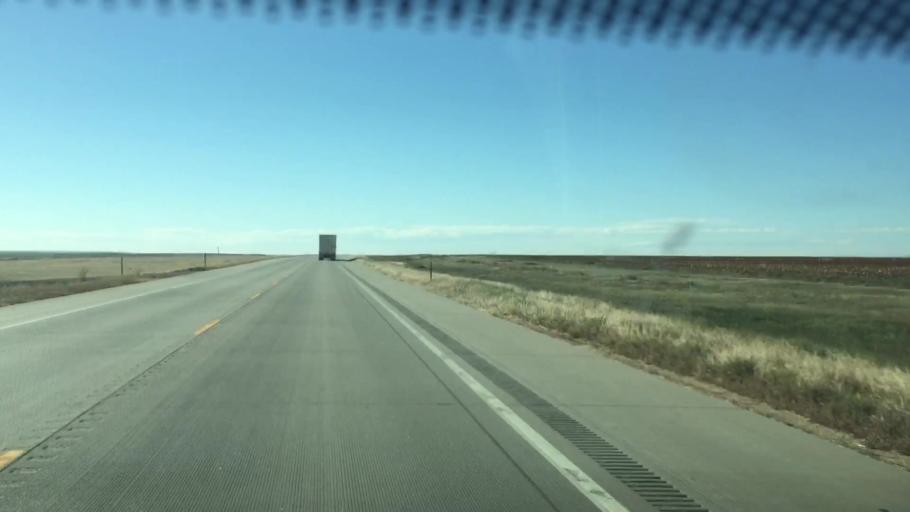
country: US
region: Colorado
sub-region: Kiowa County
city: Eads
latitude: 38.7881
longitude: -102.9272
